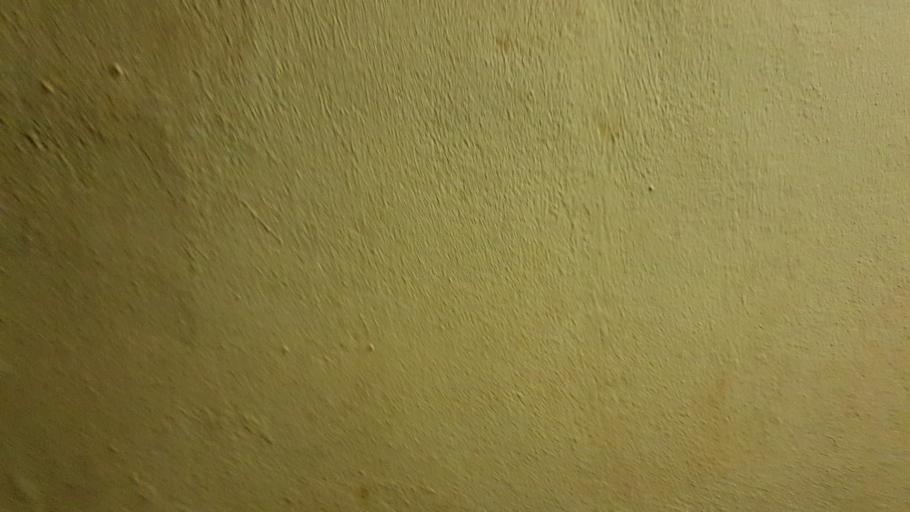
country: ML
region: Bamako
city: Bamako
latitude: 12.5609
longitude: -7.9947
